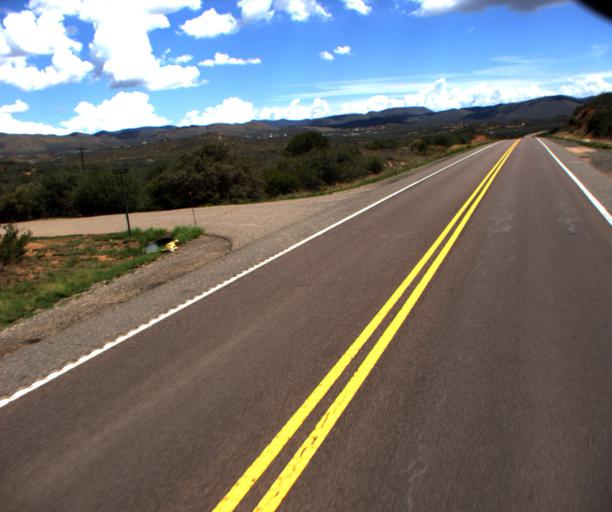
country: US
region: Arizona
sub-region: Yavapai County
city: Dewey-Humboldt
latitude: 34.5443
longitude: -112.1836
